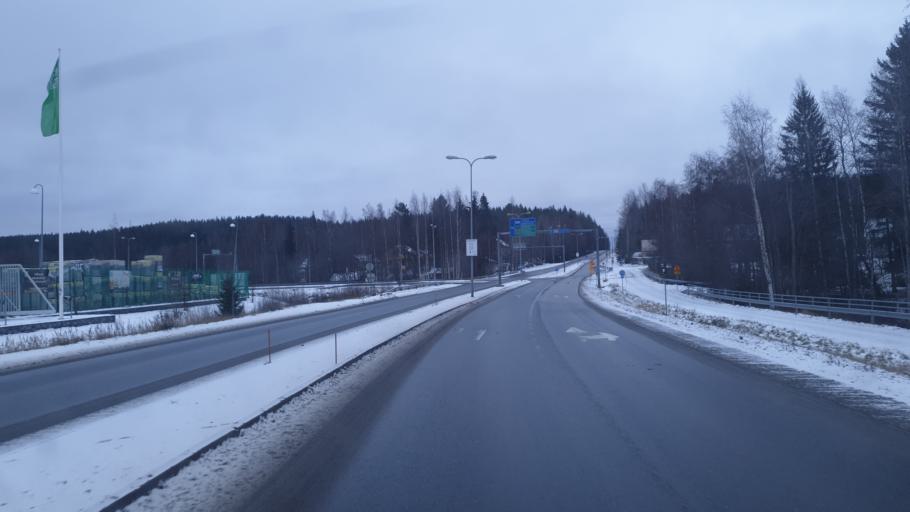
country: FI
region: Northern Savo
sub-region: Kuopio
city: Kuopio
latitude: 62.8383
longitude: 27.6104
